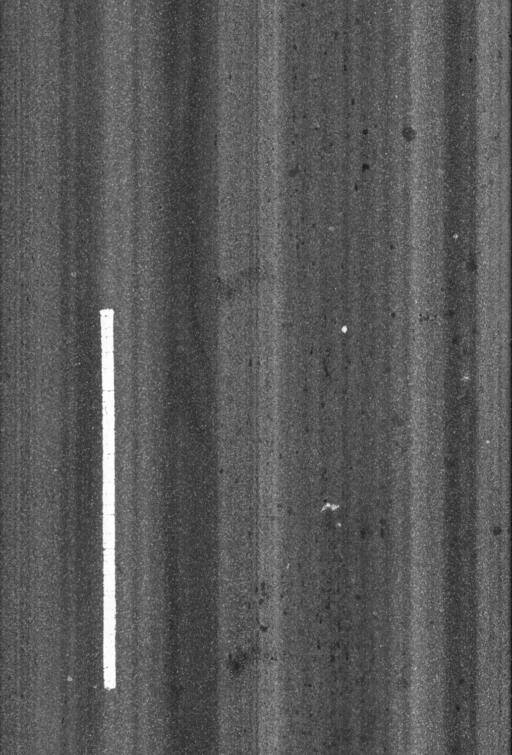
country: US
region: Maryland
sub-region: Prince George's County
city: Glassmanor
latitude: 38.8307
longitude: -76.9892
